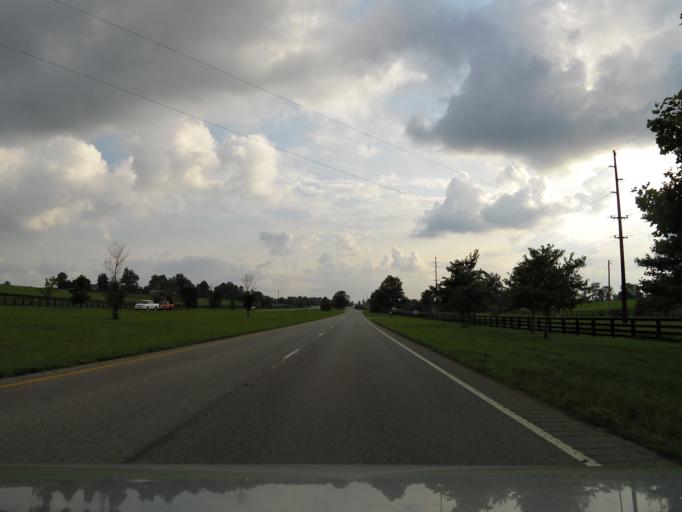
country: US
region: Kentucky
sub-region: Fayette County
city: Lexington-Fayette
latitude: 38.1254
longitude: -84.3805
